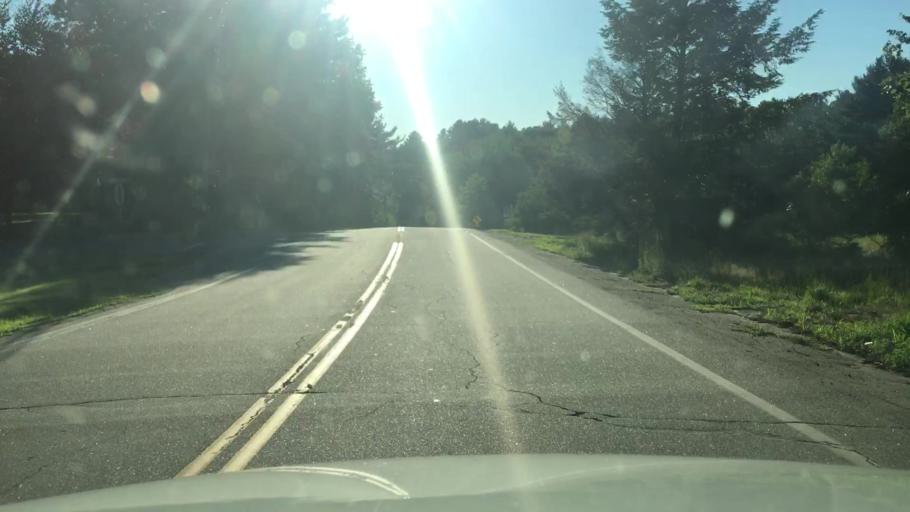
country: US
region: New Hampshire
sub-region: Rockingham County
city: Sandown
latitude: 42.9209
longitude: -71.1712
